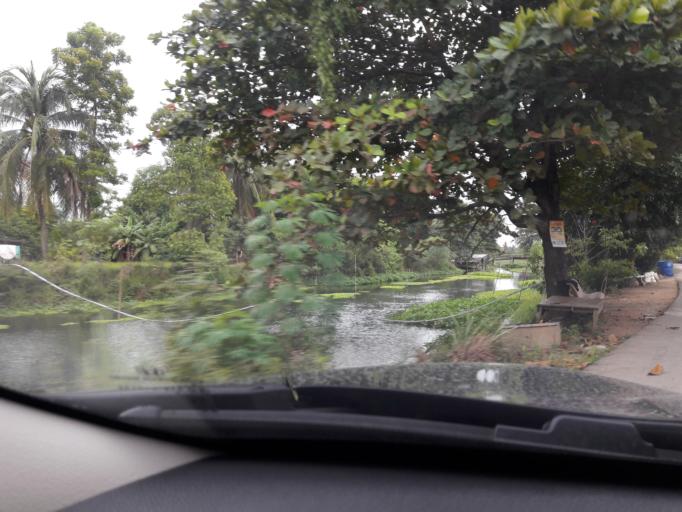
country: TH
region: Ratchaburi
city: Damnoen Saduak
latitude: 13.6031
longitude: 99.9731
